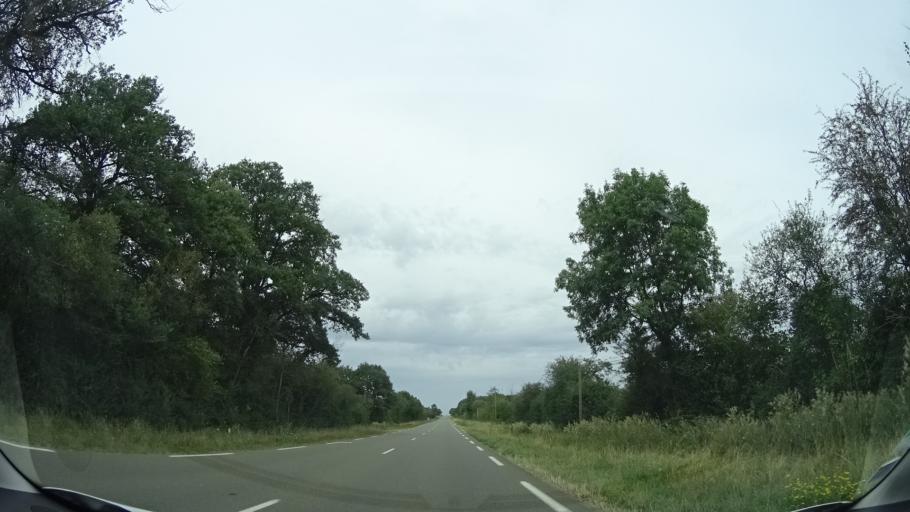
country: FR
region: Pays de la Loire
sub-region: Departement de la Mayenne
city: Meslay-du-Maine
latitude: 47.9903
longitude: -0.6272
